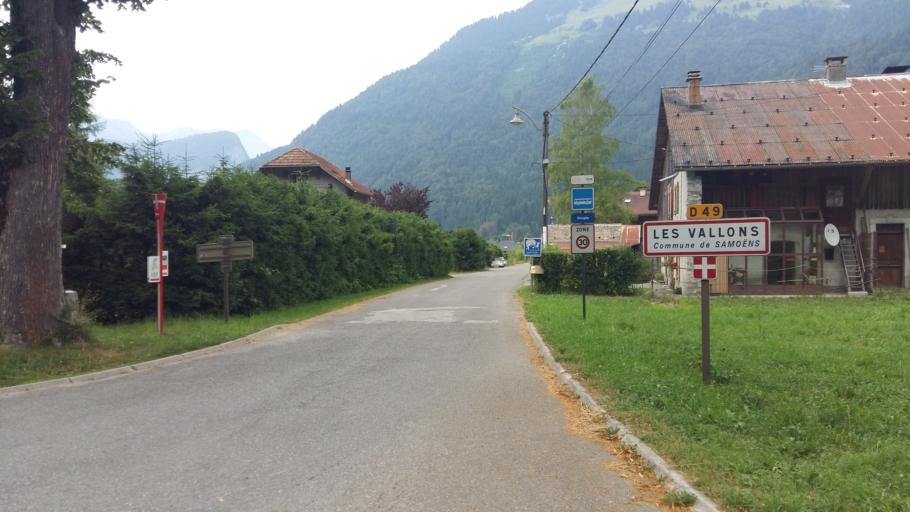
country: FR
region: Rhone-Alpes
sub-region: Departement de la Haute-Savoie
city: Samoens
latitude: 46.0637
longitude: 6.7451
